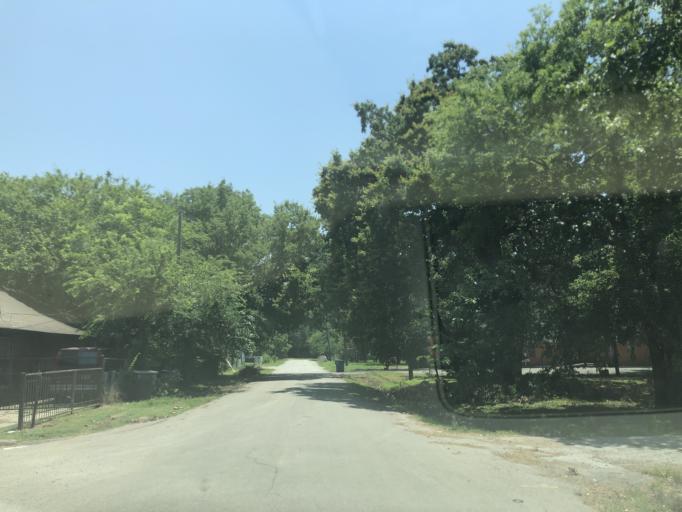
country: US
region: Texas
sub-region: Dallas County
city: Dallas
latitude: 32.7760
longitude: -96.8412
